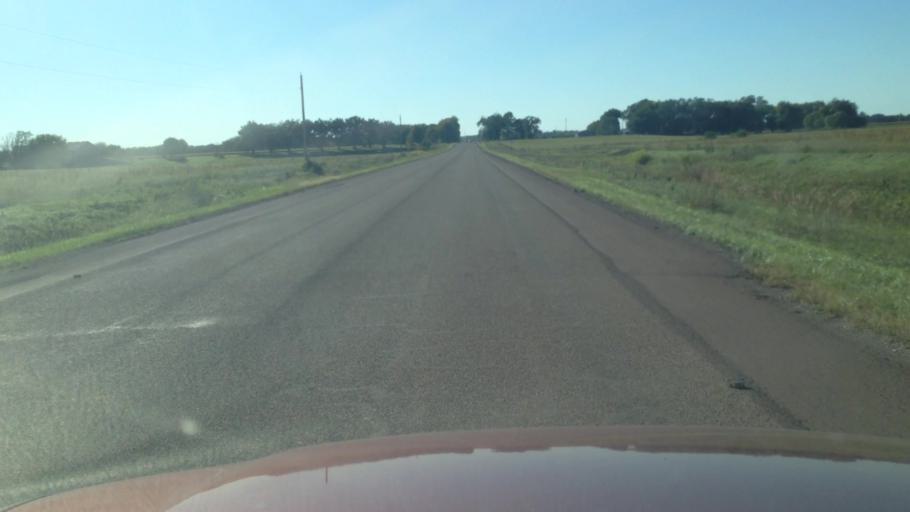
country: US
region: Kansas
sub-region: Douglas County
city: Eudora
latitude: 38.9424
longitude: -95.1506
